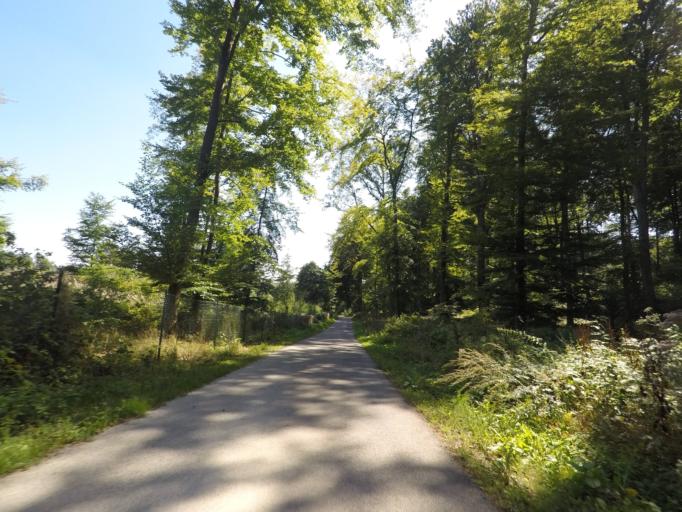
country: LU
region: Luxembourg
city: Bereldange
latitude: 49.6482
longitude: 6.1111
